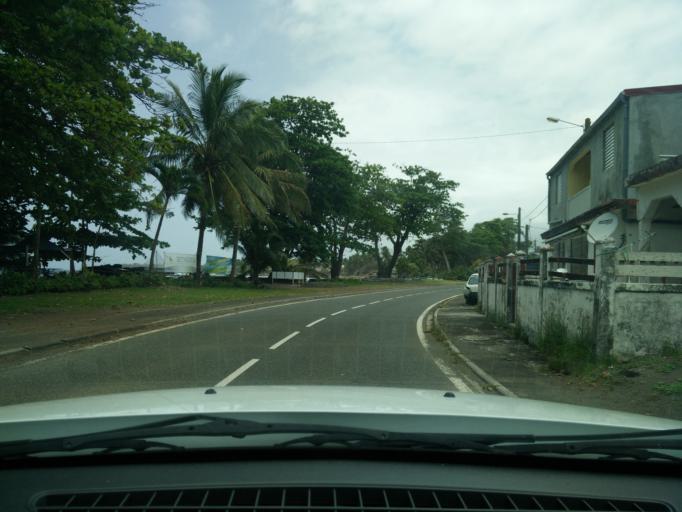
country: GP
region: Guadeloupe
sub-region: Guadeloupe
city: Capesterre-Belle-Eau
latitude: 16.0505
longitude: -61.5579
